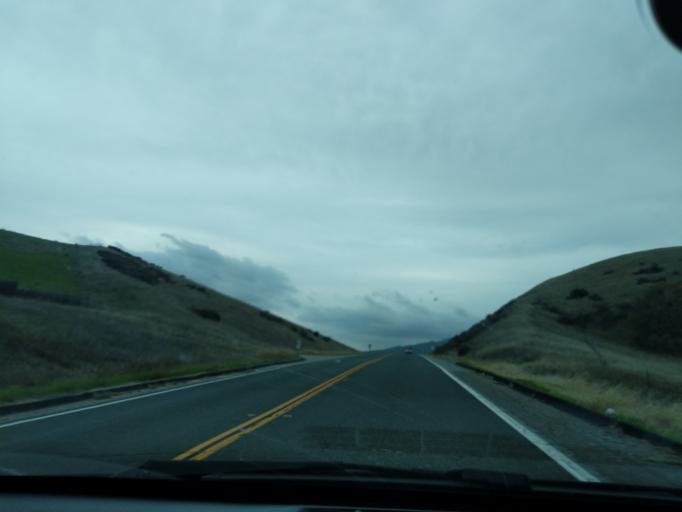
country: US
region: California
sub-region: San Benito County
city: Ridgemark
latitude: 36.6516
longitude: -121.2394
